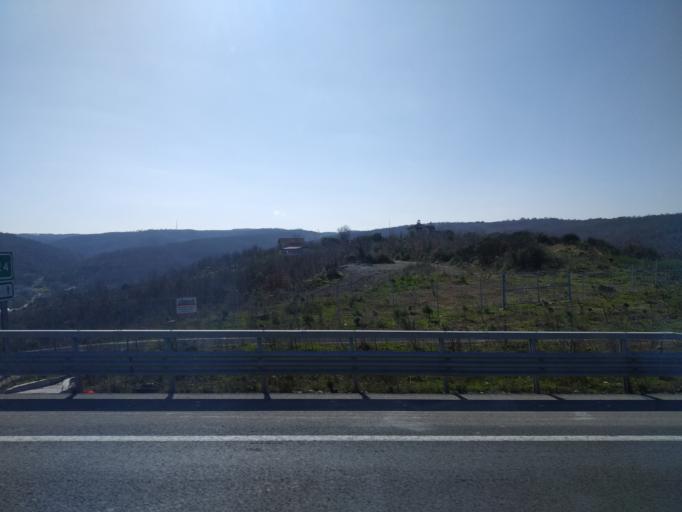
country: TR
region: Istanbul
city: Mahmut Sevket Pasa
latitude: 41.1824
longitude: 29.2307
